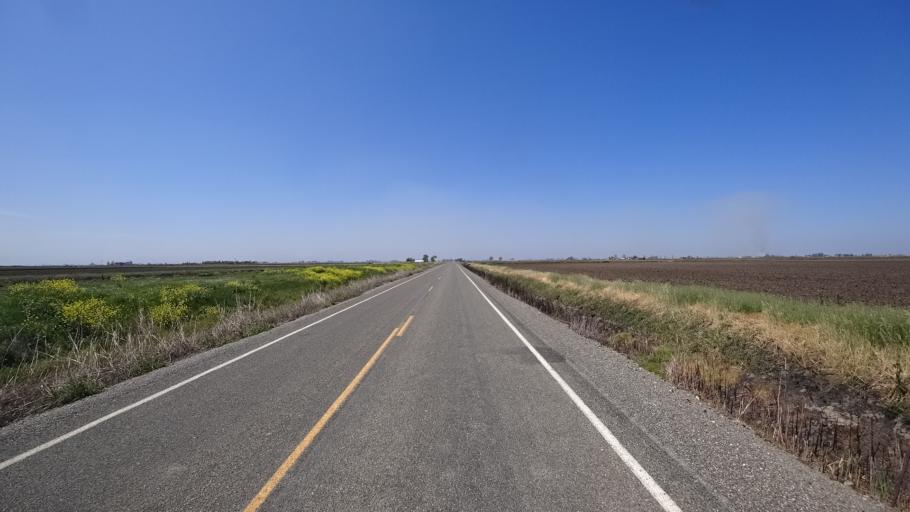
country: US
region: California
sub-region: Glenn County
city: Willows
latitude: 39.5581
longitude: -122.0390
